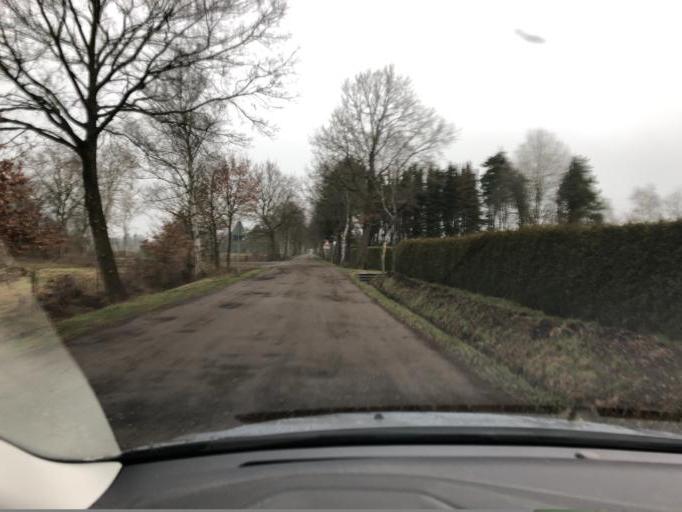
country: DE
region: Lower Saxony
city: Bad Zwischenahn
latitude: 53.1677
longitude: 8.0308
